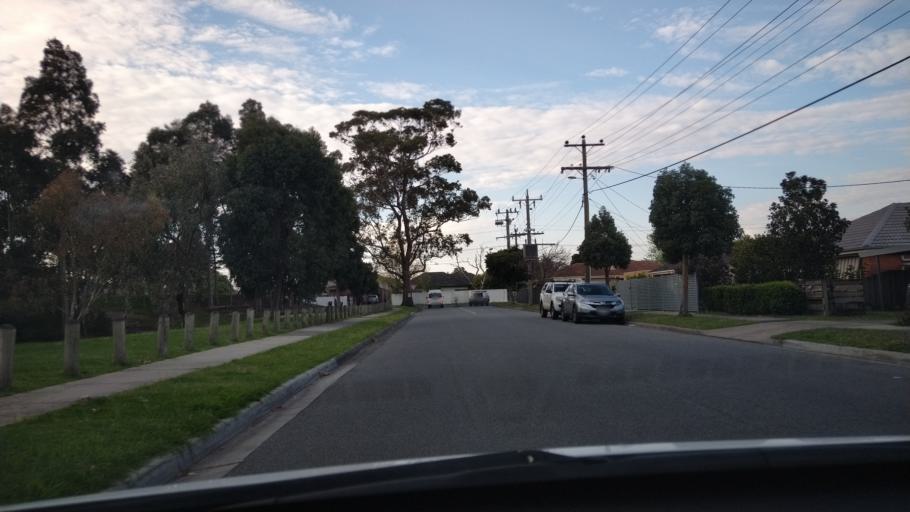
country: AU
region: Victoria
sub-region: Greater Dandenong
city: Springvale South
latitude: -37.9637
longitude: 145.1547
